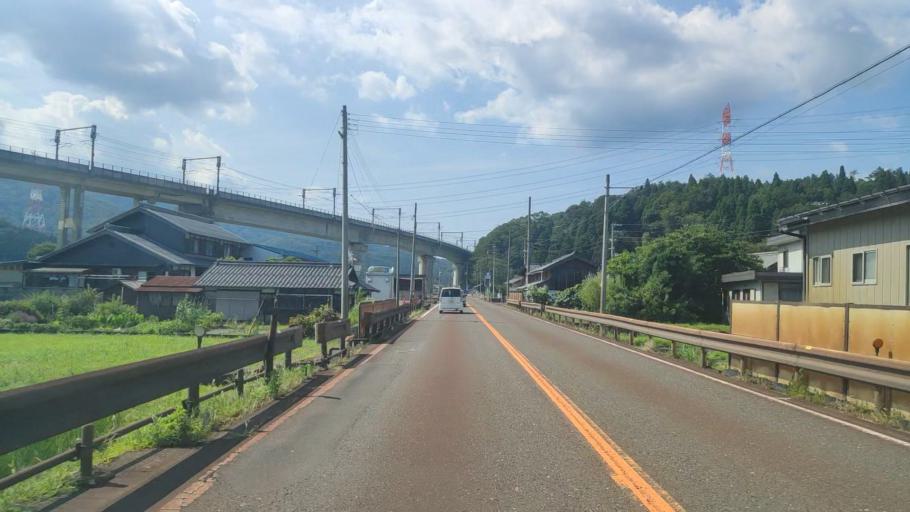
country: JP
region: Fukui
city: Tsuruga
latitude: 35.5296
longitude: 136.1563
